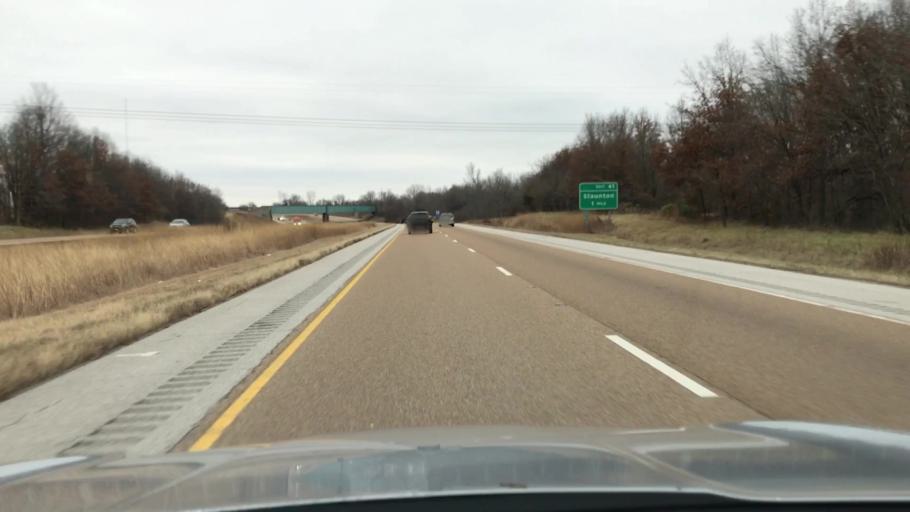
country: US
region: Illinois
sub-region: Macoupin County
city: Mount Olive
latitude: 39.0403
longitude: -89.7558
